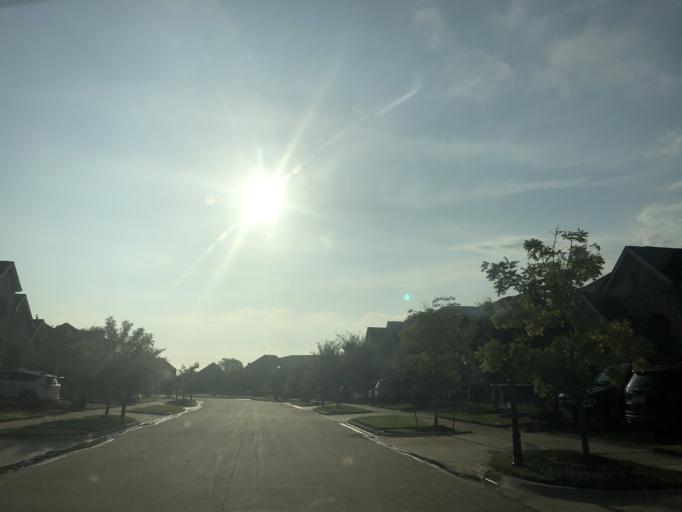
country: US
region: Texas
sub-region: Tarrant County
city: Euless
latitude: 32.8430
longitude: -97.0705
